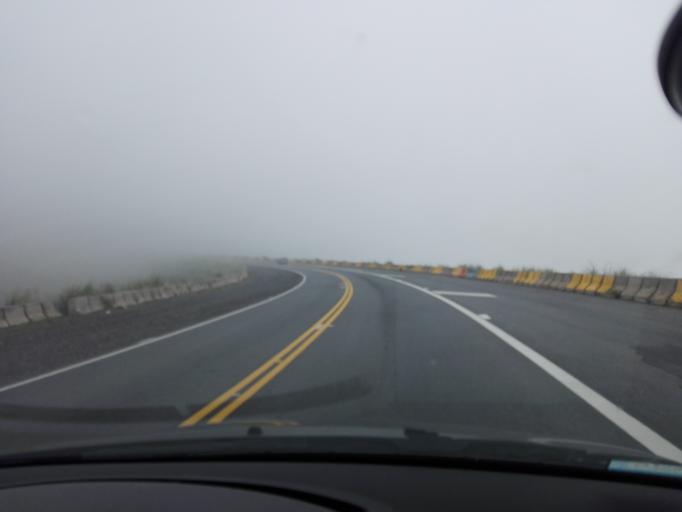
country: AR
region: Cordoba
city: Cuesta Blanca
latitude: -31.5961
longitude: -64.7122
